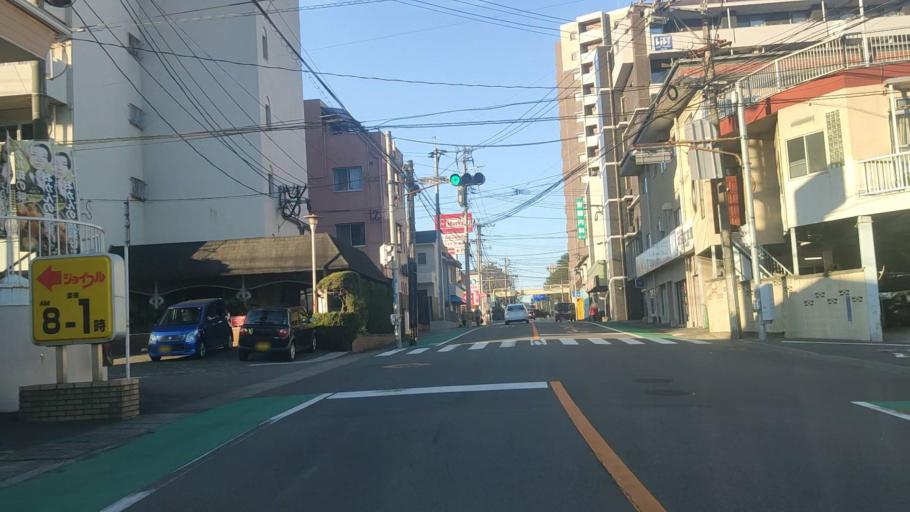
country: JP
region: Oita
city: Beppu
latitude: 33.2783
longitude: 131.4893
